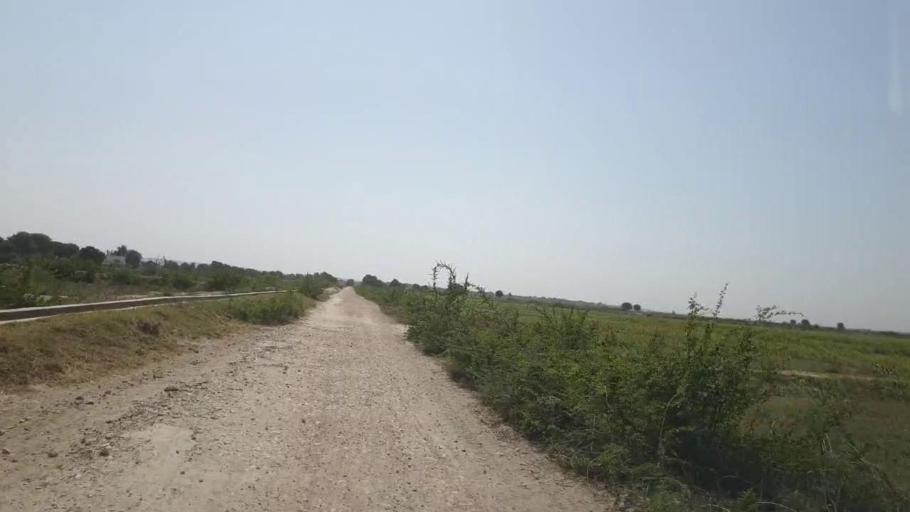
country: PK
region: Sindh
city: Naukot
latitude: 24.9022
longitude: 69.4875
